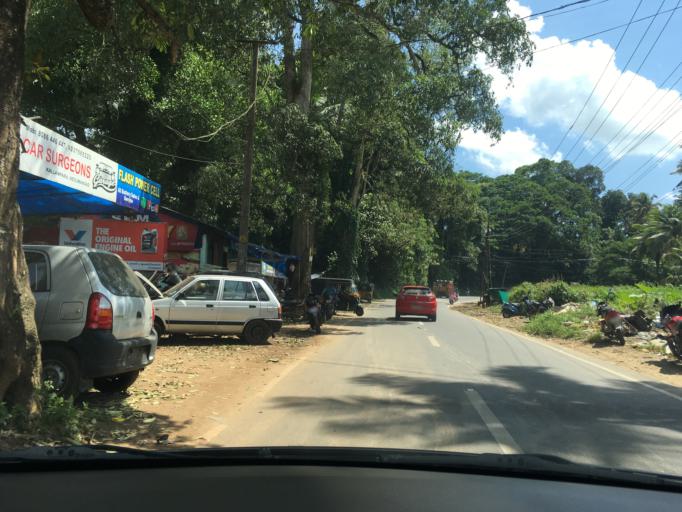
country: IN
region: Kerala
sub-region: Thiruvananthapuram
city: Nedumangad
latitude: 8.6072
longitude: 76.9991
